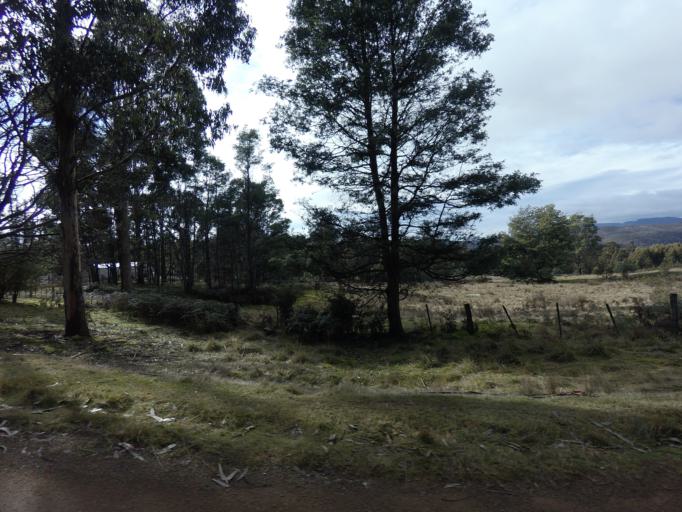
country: AU
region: Tasmania
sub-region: Derwent Valley
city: New Norfolk
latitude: -42.7873
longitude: 146.9175
